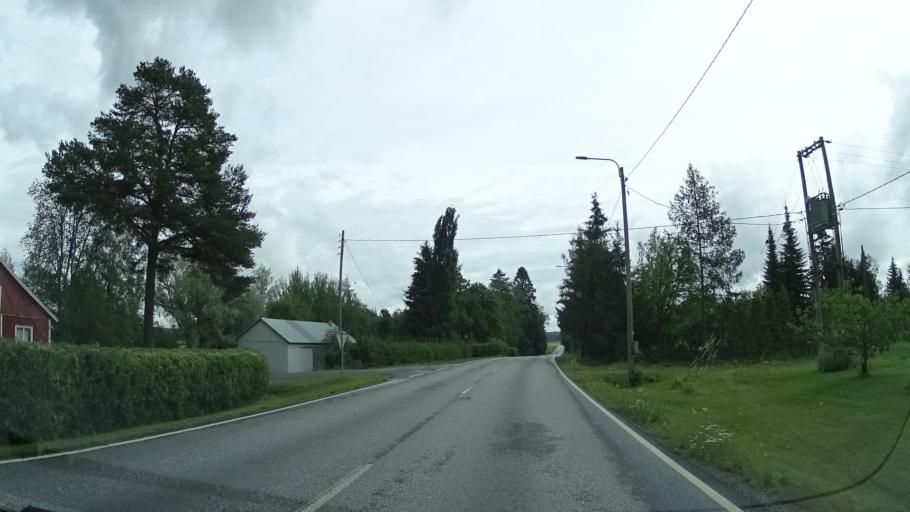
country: FI
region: Haeme
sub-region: Forssa
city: Humppila
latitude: 61.1015
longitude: 23.2865
